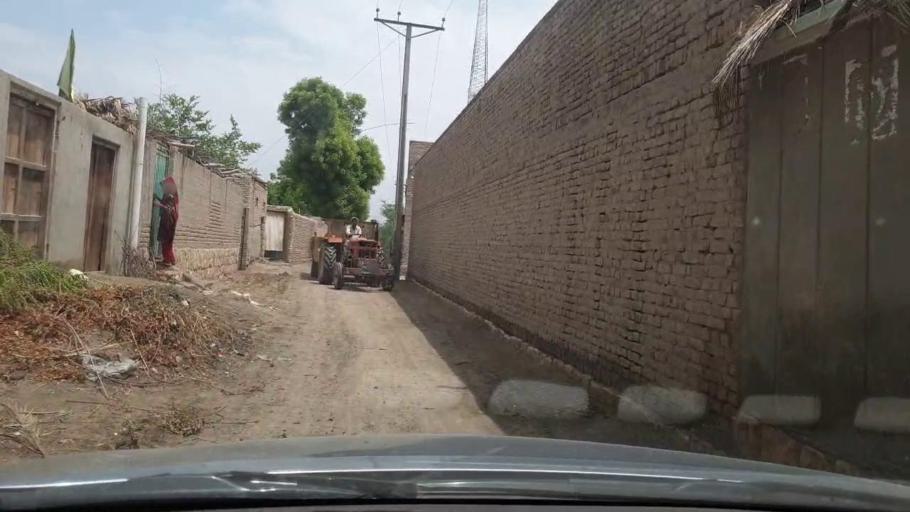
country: PK
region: Sindh
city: Kot Diji
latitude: 27.4290
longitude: 68.7528
